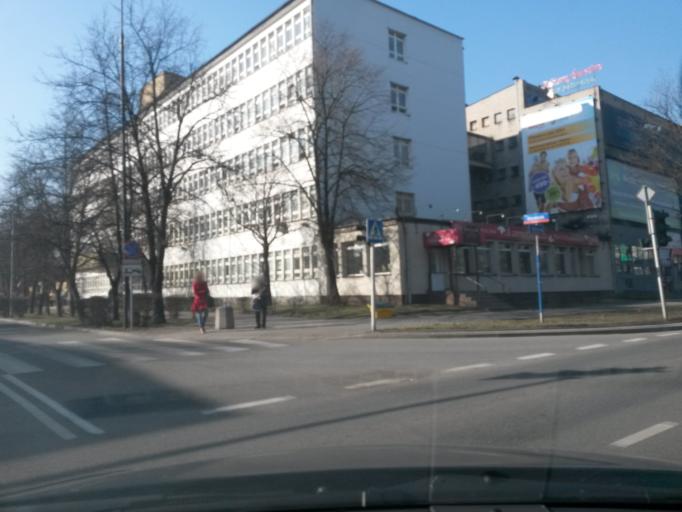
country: PL
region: Masovian Voivodeship
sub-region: Warszawa
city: Ochota
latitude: 52.1800
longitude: 20.9940
